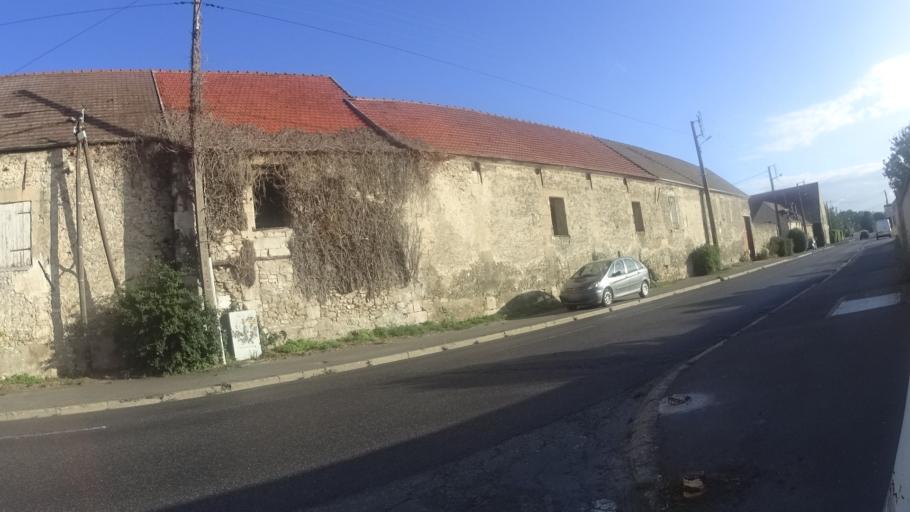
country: FR
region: Picardie
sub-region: Departement de l'Oise
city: Pontpoint
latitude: 49.2758
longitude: 2.6915
